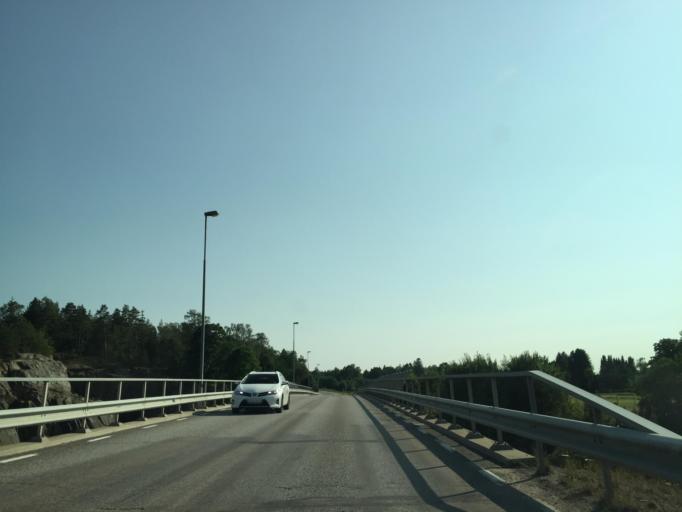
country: SE
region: Vaestra Goetaland
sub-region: Trollhattan
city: Trollhattan
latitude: 58.3266
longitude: 12.2619
